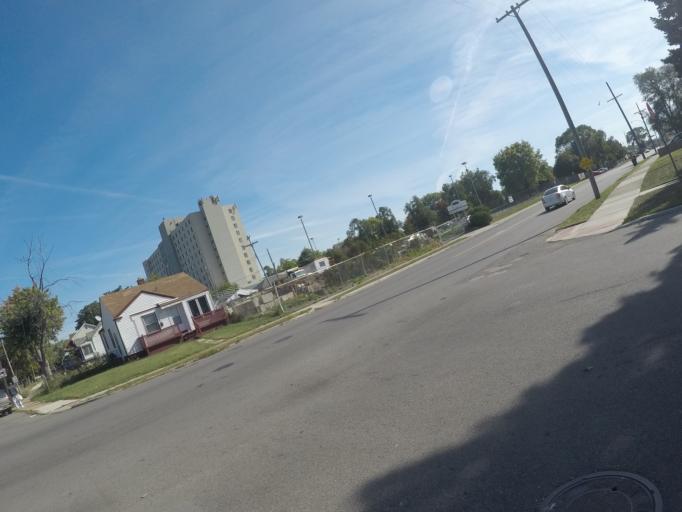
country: US
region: Michigan
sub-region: Wayne County
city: Melvindale
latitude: 42.2669
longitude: -83.1587
